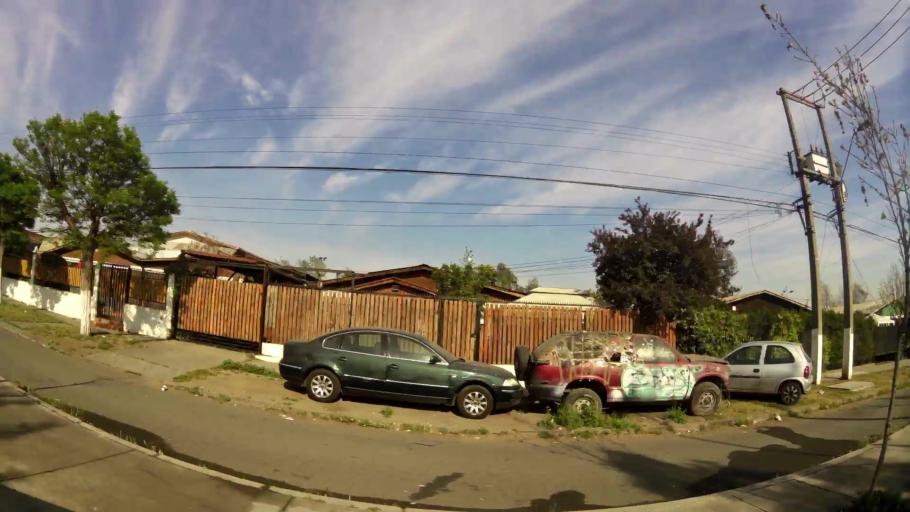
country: CL
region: Santiago Metropolitan
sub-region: Provincia de Santiago
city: Santiago
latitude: -33.5121
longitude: -70.6376
